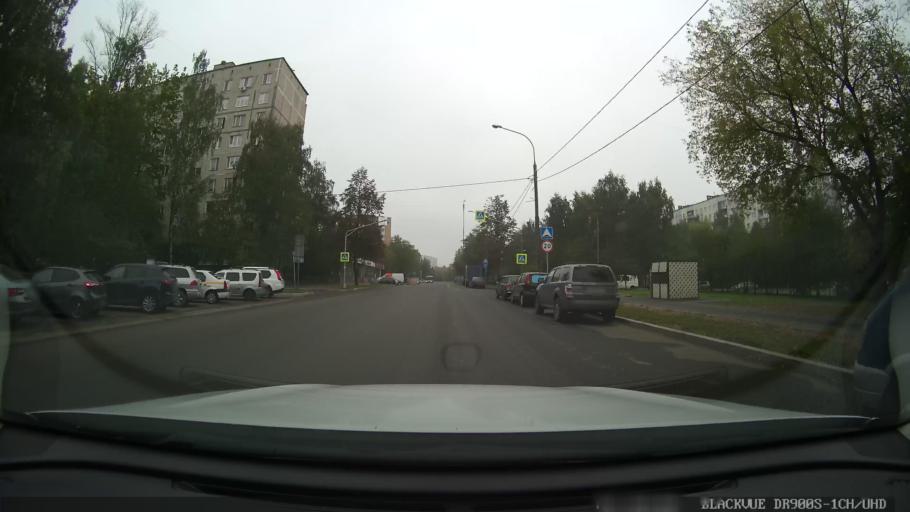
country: RU
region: Moscow
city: Kolomenskoye
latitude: 55.6695
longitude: 37.6488
